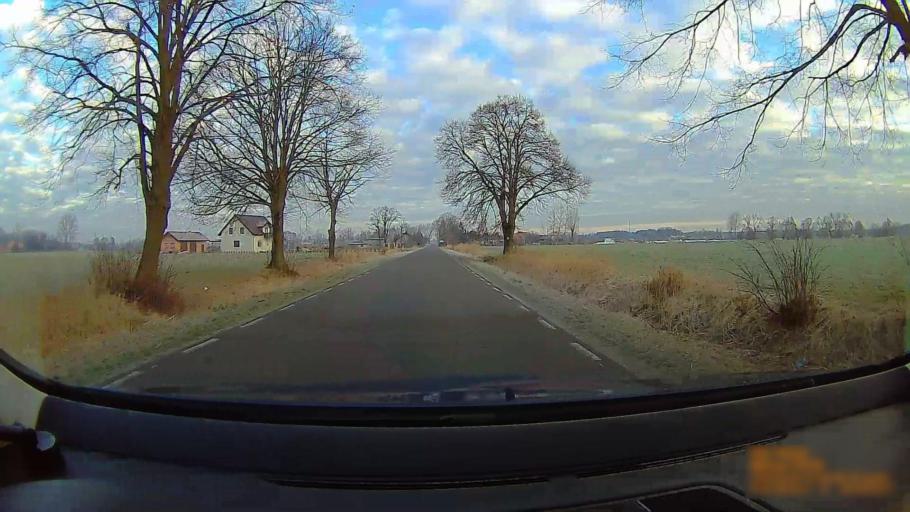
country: PL
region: Greater Poland Voivodeship
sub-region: Powiat koninski
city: Rzgow Pierwszy
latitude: 52.1419
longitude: 18.0561
